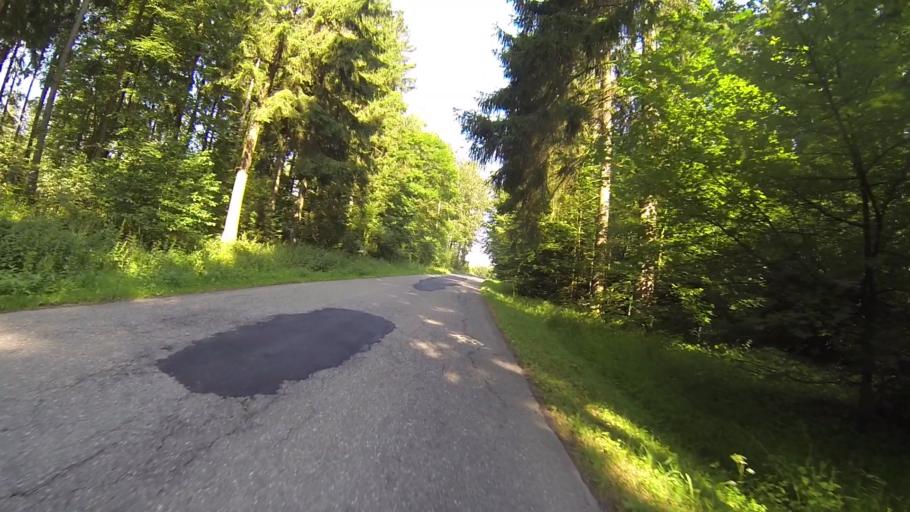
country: DE
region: Baden-Wuerttemberg
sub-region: Regierungsbezirk Stuttgart
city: Konigsbronn
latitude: 48.7504
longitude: 10.1310
